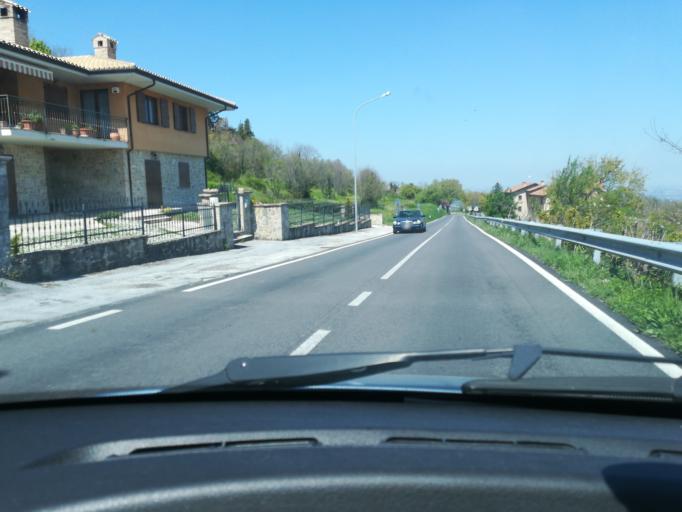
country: IT
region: The Marches
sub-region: Provincia di Macerata
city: Cingoli
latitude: 43.3765
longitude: 13.2176
